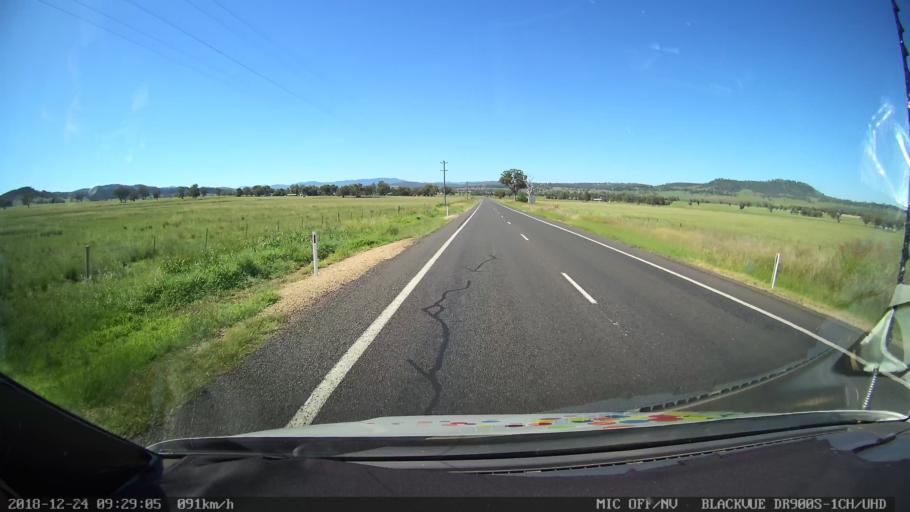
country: AU
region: New South Wales
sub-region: Liverpool Plains
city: Quirindi
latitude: -31.5458
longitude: 150.6925
